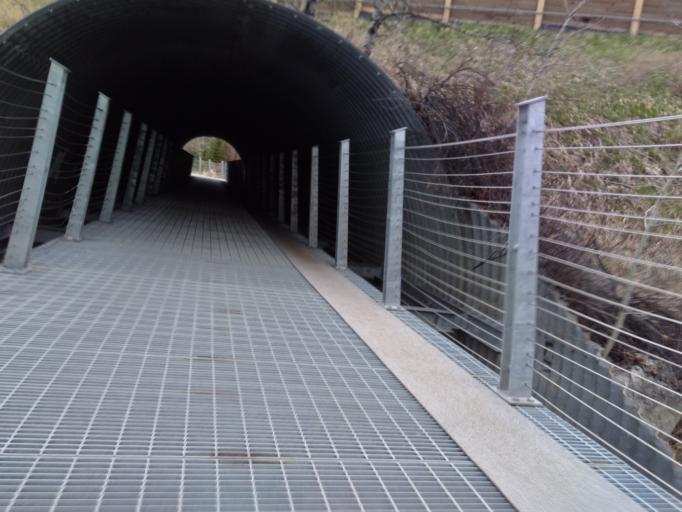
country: CA
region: Alberta
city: Cochrane
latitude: 51.1828
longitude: -114.4807
